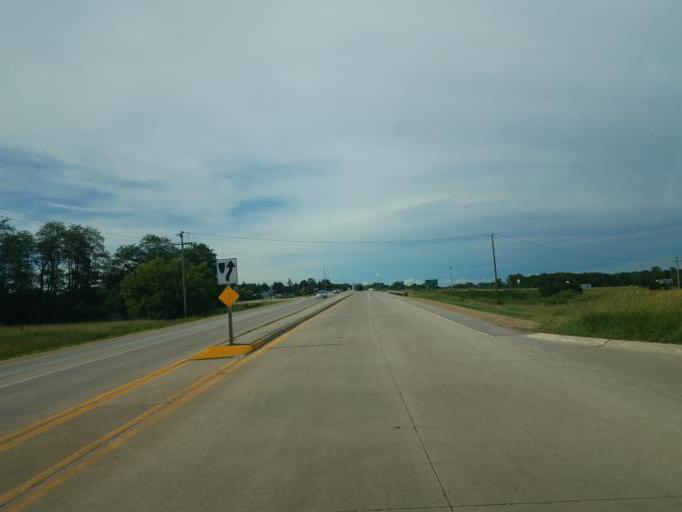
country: US
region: Wisconsin
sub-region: Monroe County
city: Tomah
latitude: 43.9548
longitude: -90.5047
